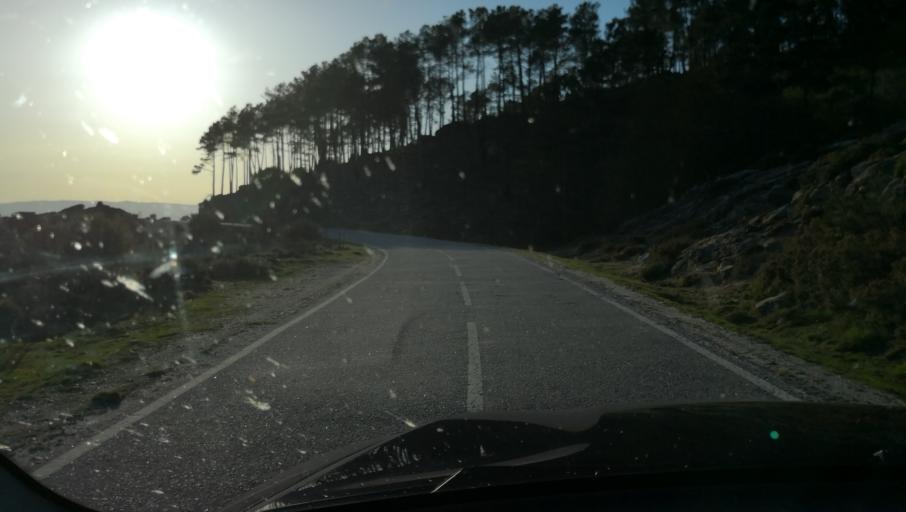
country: PT
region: Vila Real
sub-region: Vila Real
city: Vila Real
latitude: 41.3872
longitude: -7.8242
